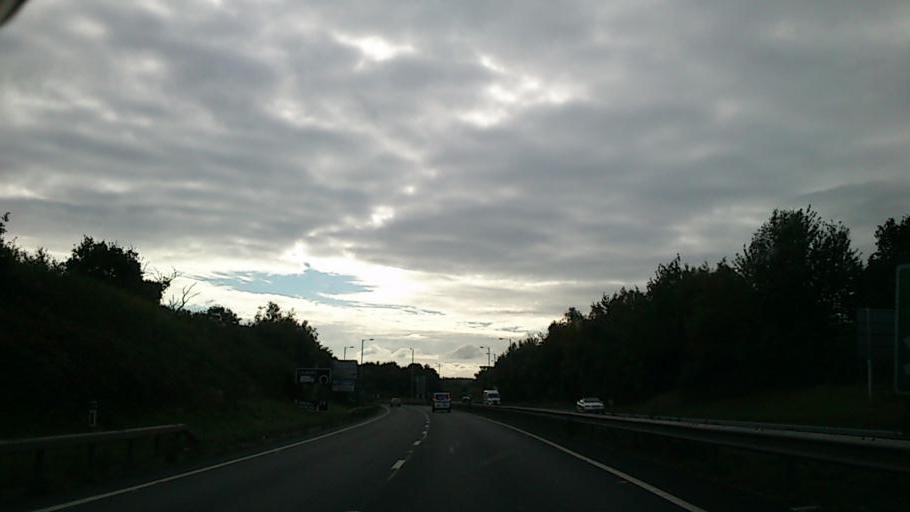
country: GB
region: England
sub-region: Shropshire
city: Great Hanwood
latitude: 52.6923
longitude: -2.8045
